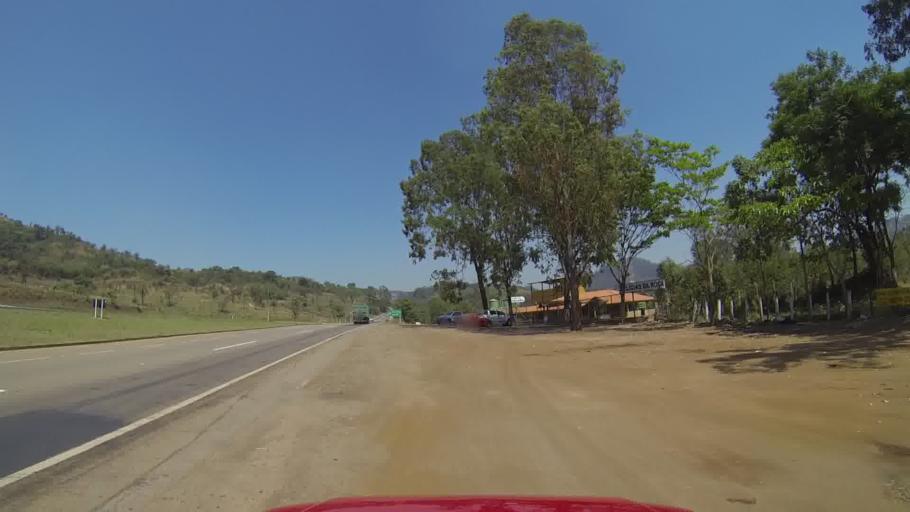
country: BR
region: Minas Gerais
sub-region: Itauna
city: Itauna
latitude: -20.0268
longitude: -44.5109
